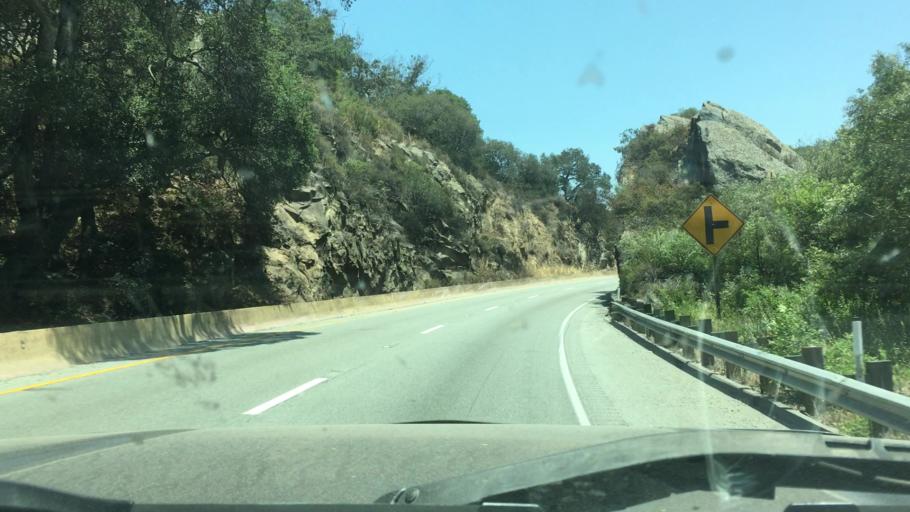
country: US
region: California
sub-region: San Benito County
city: Aromas
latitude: 36.8596
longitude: -121.6293
